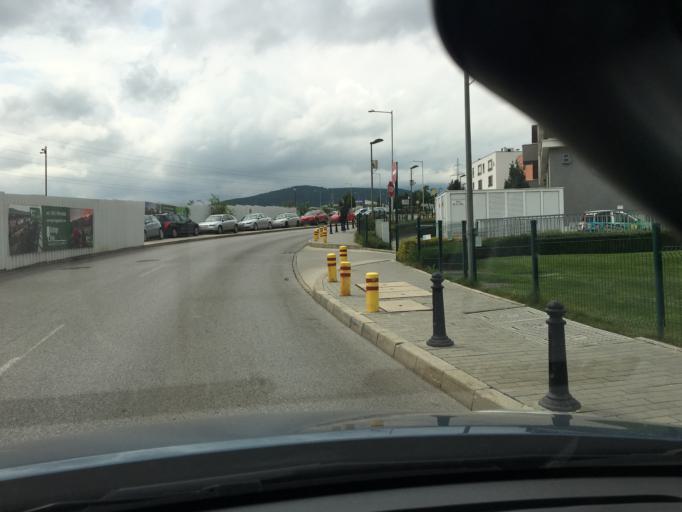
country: BG
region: Sofia-Capital
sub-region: Stolichna Obshtina
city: Sofia
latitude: 42.6211
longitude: 23.3697
